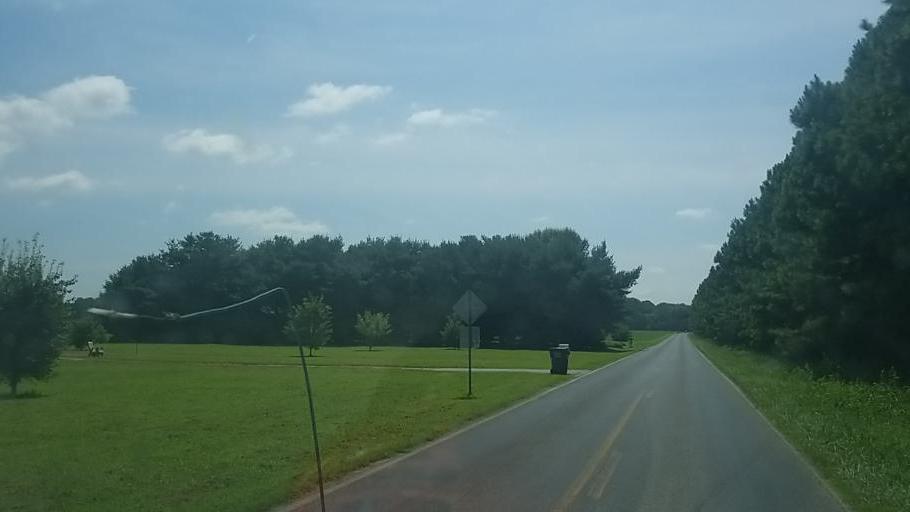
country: US
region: Maryland
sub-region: Caroline County
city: Ridgely
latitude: 38.8895
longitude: -75.9279
